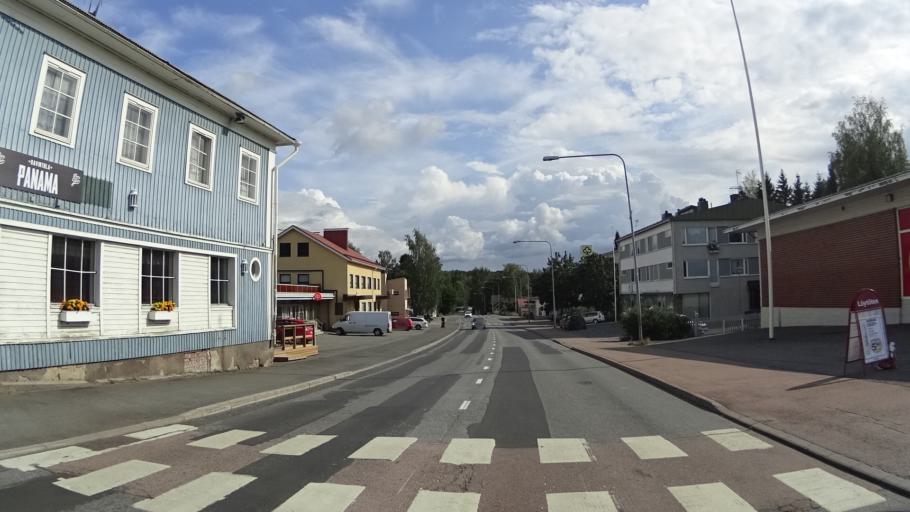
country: FI
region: Pirkanmaa
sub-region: Tampere
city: Paelkaene
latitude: 61.3370
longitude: 24.2695
